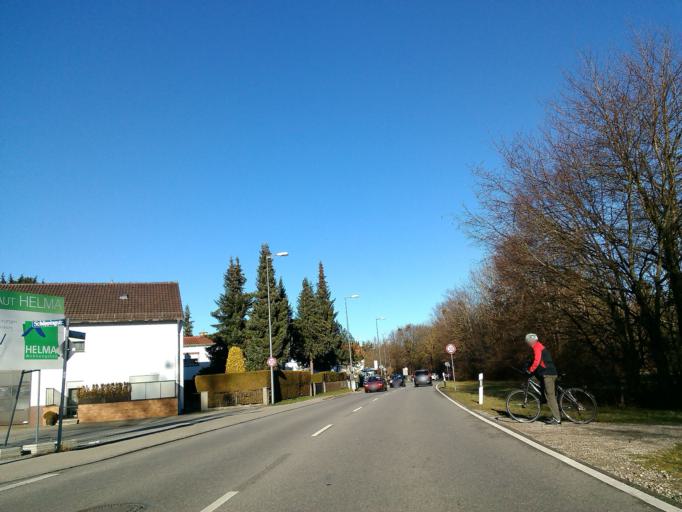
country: DE
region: Bavaria
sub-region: Upper Bavaria
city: Pasing
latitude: 48.1720
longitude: 11.4596
